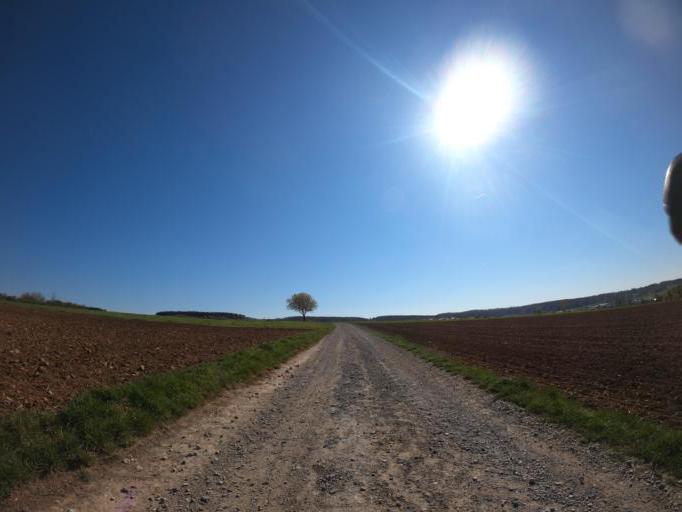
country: DE
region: Baden-Wuerttemberg
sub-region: Karlsruhe Region
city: Wiernsheim
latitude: 48.8932
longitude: 8.8664
